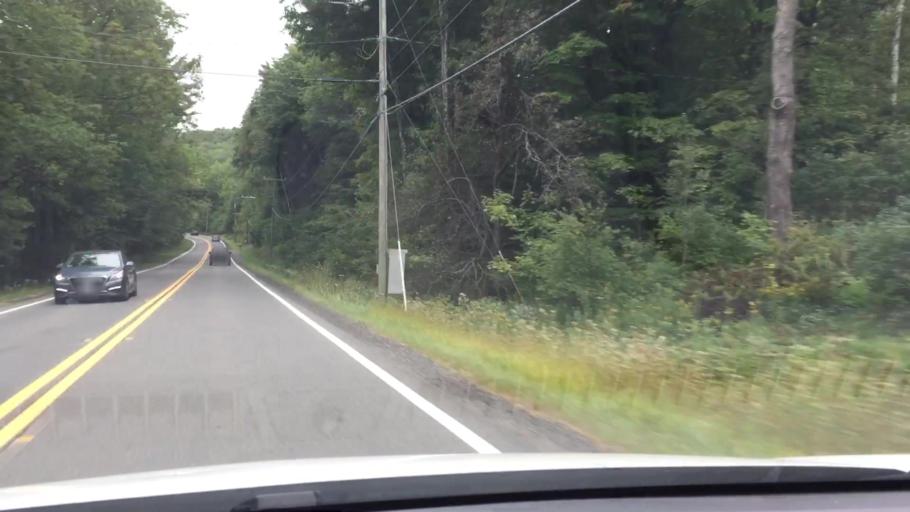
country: US
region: Massachusetts
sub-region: Berkshire County
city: Hinsdale
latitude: 42.3834
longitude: -73.1225
